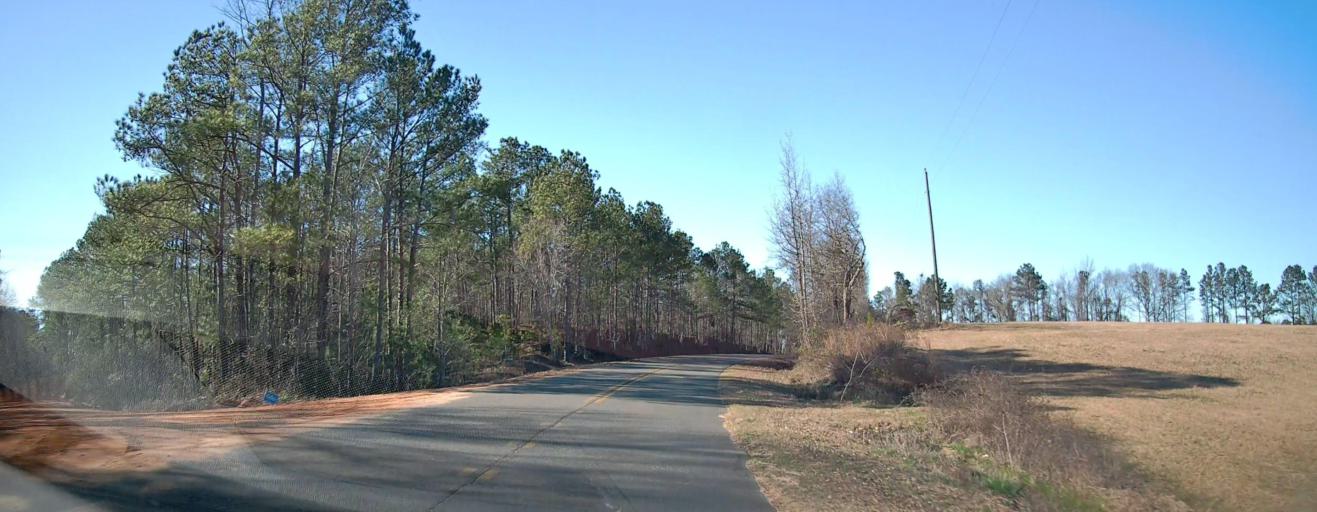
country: US
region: Georgia
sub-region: Taylor County
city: Butler
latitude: 32.6446
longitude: -84.3146
